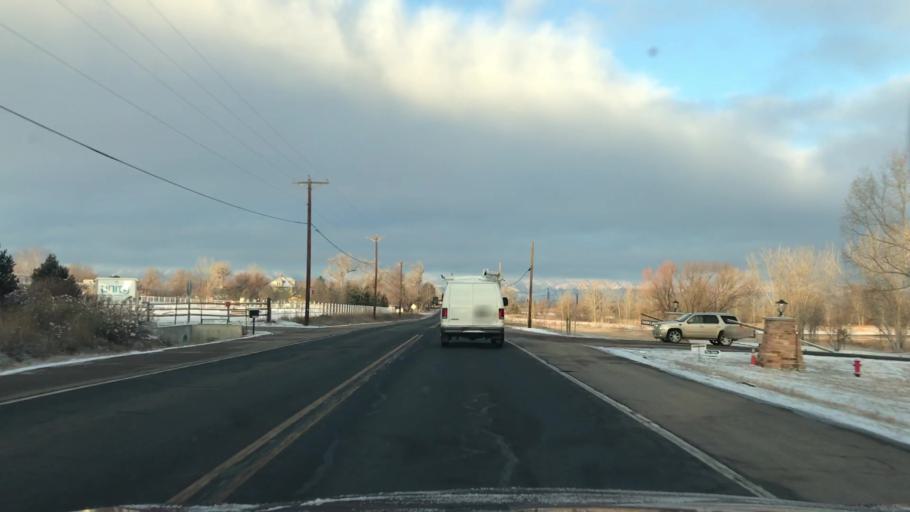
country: US
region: Colorado
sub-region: Boulder County
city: Louisville
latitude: 40.0147
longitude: -105.1460
